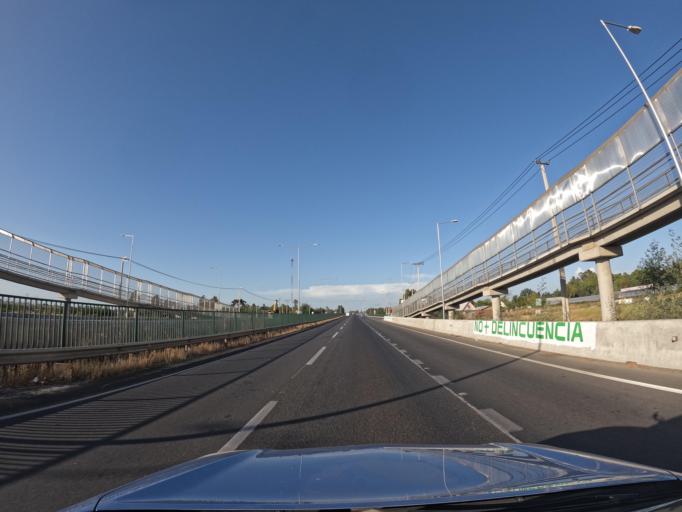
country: CL
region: Maule
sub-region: Provincia de Linares
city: Linares
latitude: -35.8687
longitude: -71.6339
